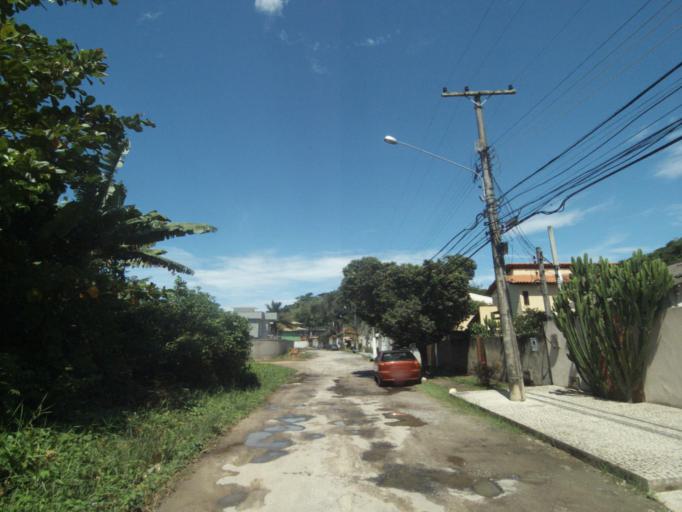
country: BR
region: Rio de Janeiro
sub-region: Niteroi
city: Niteroi
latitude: -22.9484
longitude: -43.0447
